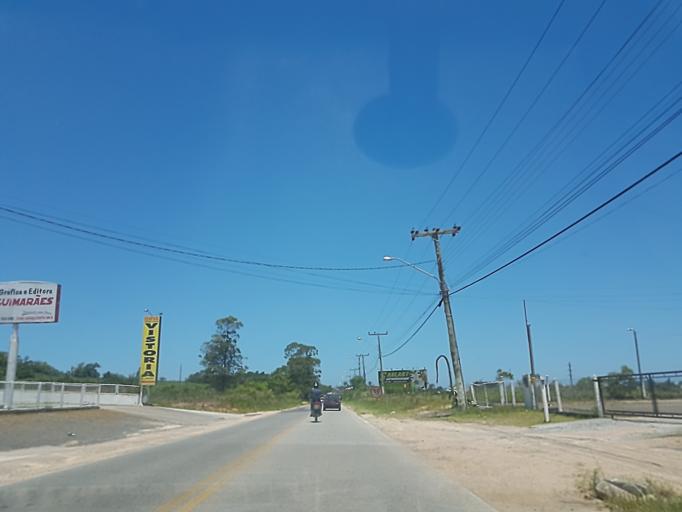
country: BR
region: Santa Catarina
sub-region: Jaguaruna
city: Jaguaruna
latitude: -28.6062
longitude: -49.0328
